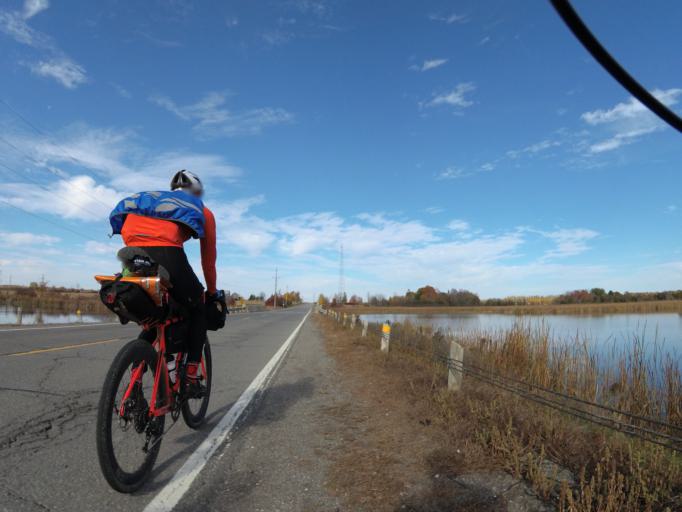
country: CA
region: Ontario
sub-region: Lanark County
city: Smiths Falls
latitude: 44.8879
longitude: -76.0069
